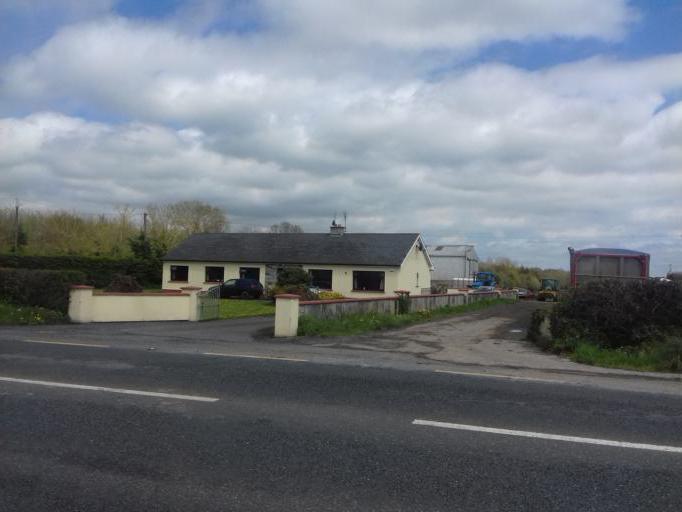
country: IE
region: Leinster
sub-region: Laois
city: Portlaoise
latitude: 53.0575
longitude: -7.3237
